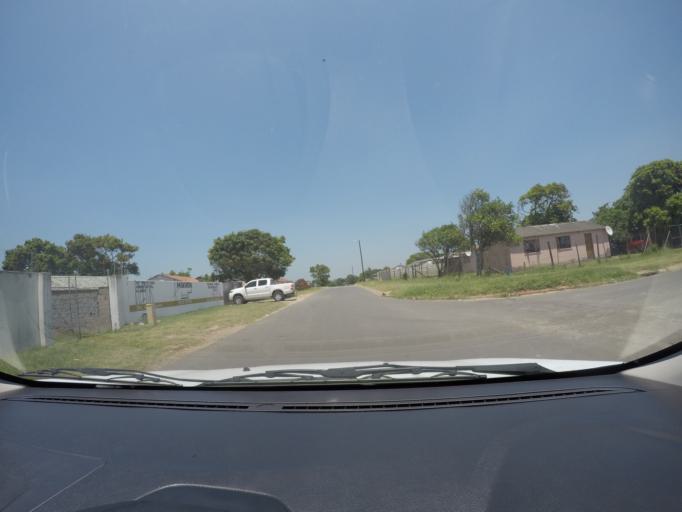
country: ZA
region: KwaZulu-Natal
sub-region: uThungulu District Municipality
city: eSikhawini
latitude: -28.8775
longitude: 31.9115
